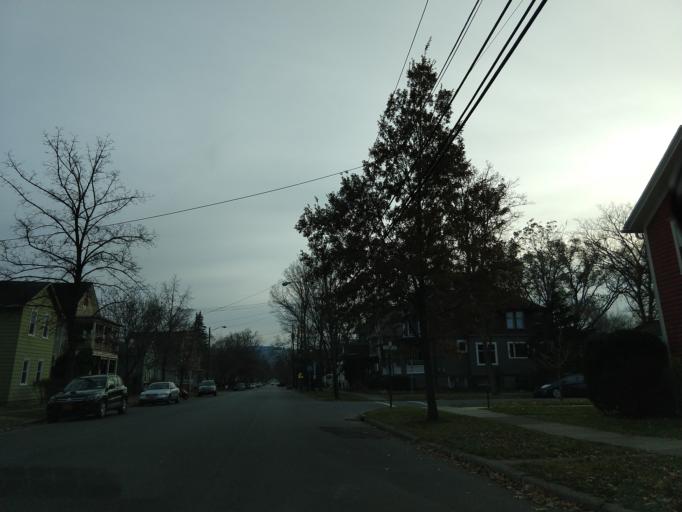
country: US
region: New York
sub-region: Tompkins County
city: Ithaca
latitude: 42.4510
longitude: -76.4975
